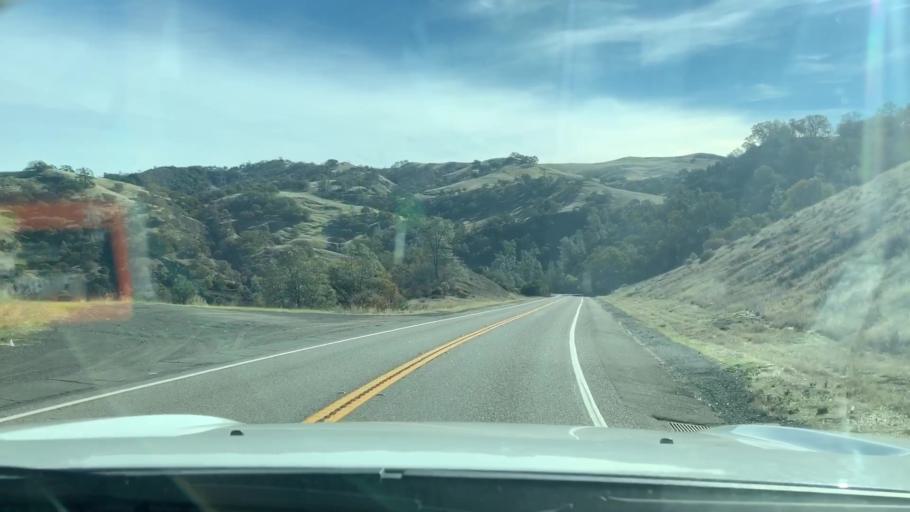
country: US
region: California
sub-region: Monterey County
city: King City
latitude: 36.1903
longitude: -120.7536
